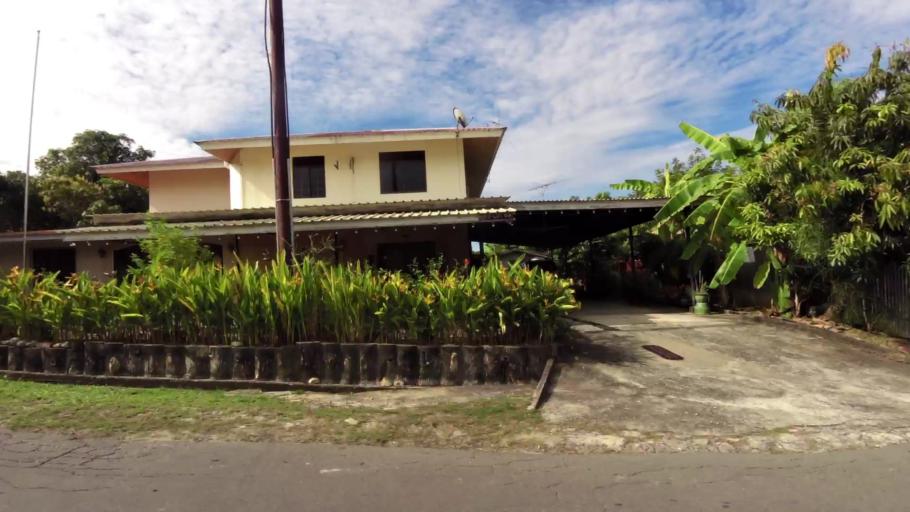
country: BN
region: Brunei and Muara
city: Bandar Seri Begawan
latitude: 4.9212
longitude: 114.8978
